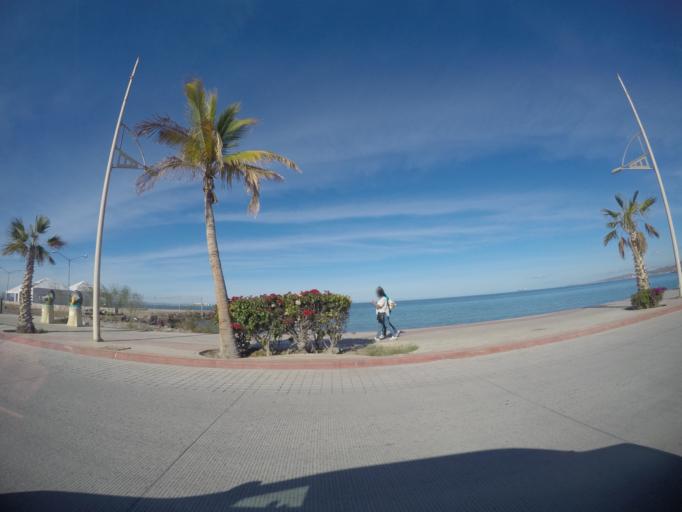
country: MX
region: Baja California Sur
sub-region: La Paz
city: La Paz
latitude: 24.1919
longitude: -110.2952
